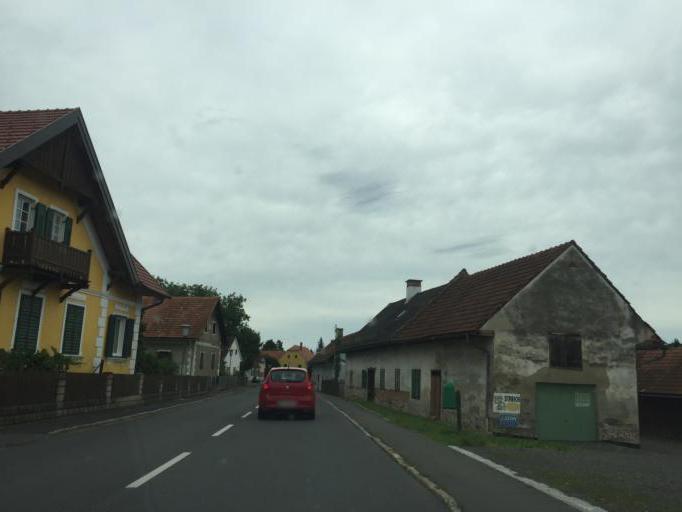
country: AT
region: Styria
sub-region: Politischer Bezirk Suedoststeiermark
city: Mureck
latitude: 46.7067
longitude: 15.7665
